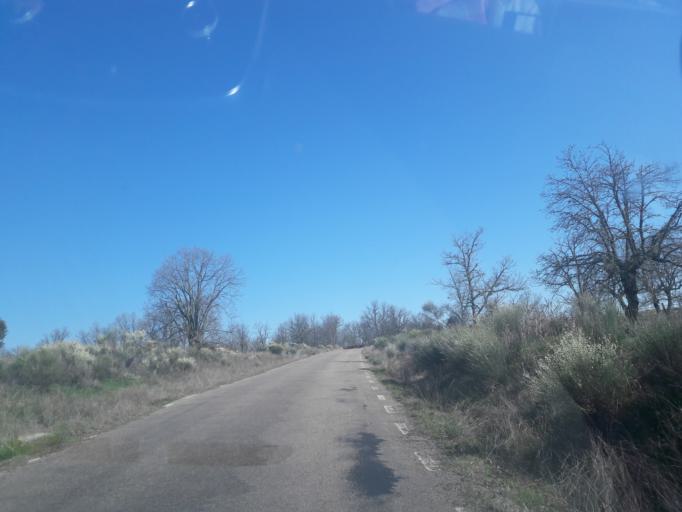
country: ES
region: Castille and Leon
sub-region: Provincia de Salamanca
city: Valsalabroso
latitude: 41.1122
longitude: -6.4837
